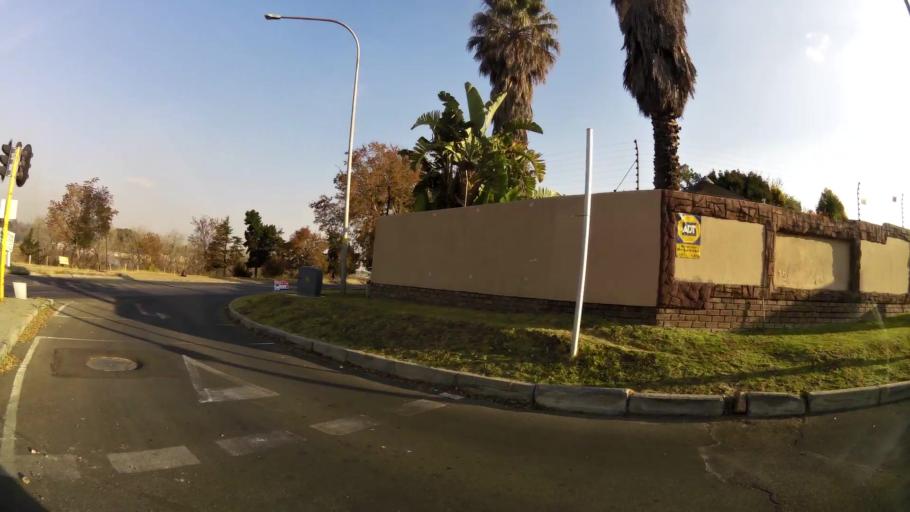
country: ZA
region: Gauteng
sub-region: City of Johannesburg Metropolitan Municipality
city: Modderfontein
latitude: -26.0757
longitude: 28.2239
